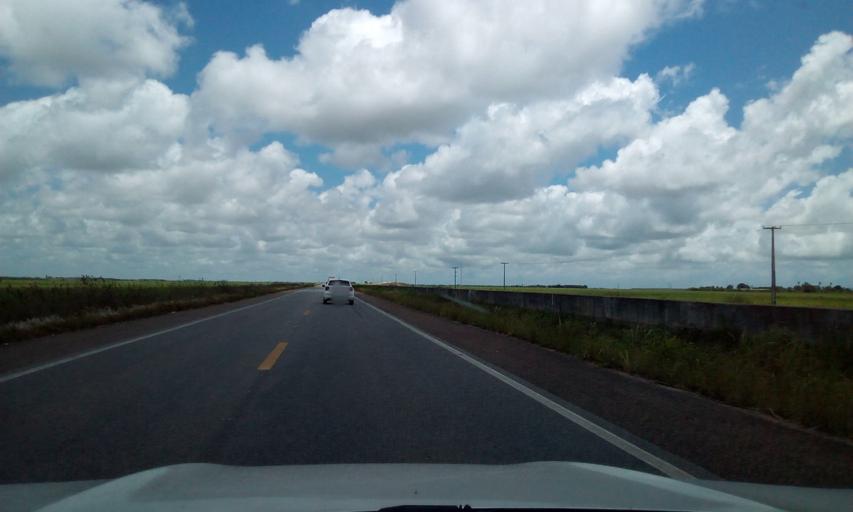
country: BR
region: Alagoas
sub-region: Sao Miguel Dos Campos
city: Sao Miguel dos Campos
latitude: -9.8956
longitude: -36.2005
